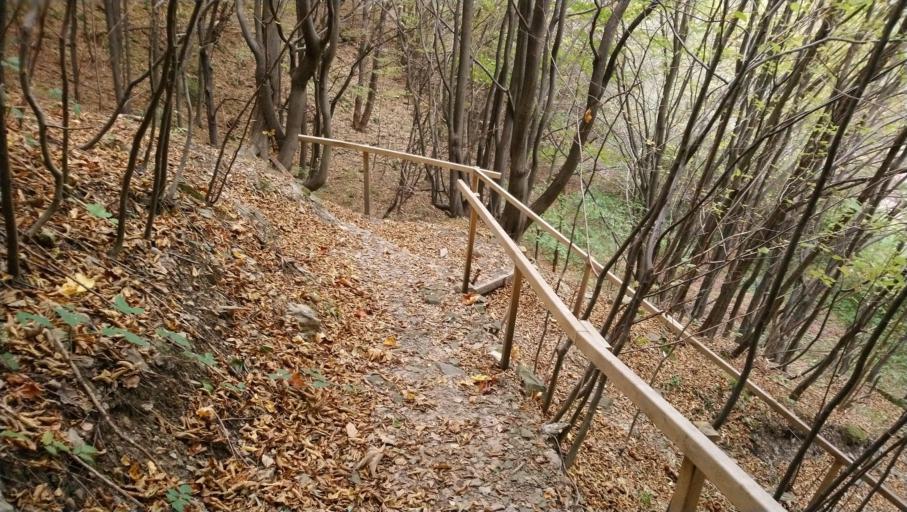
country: PL
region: Lesser Poland Voivodeship
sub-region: Powiat gorlicki
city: Ropa
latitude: 49.5606
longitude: 21.0829
